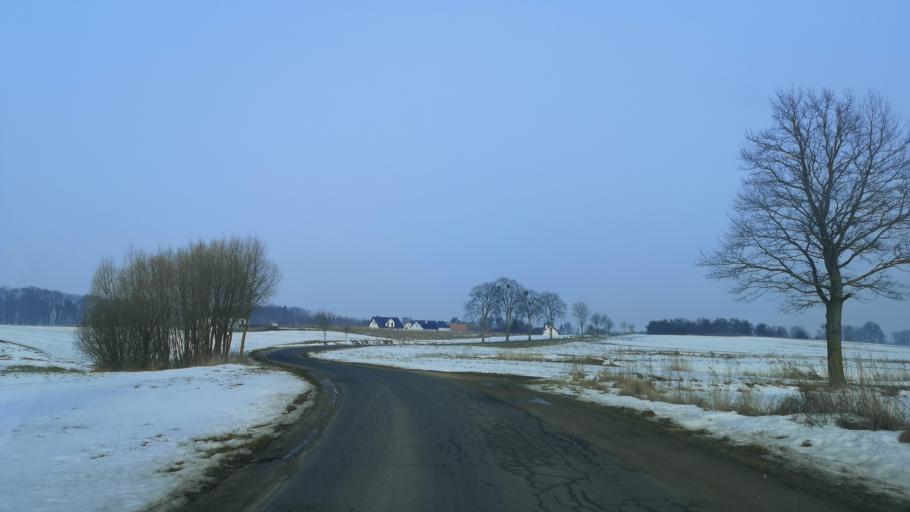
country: PL
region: Warmian-Masurian Voivodeship
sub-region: Powiat nowomiejski
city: Biskupiec
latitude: 53.4962
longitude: 19.3252
